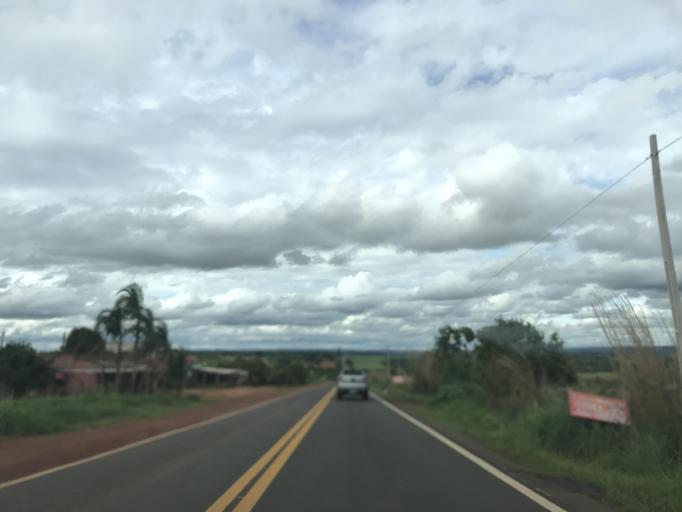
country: BR
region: Goias
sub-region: Piracanjuba
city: Piracanjuba
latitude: -17.2015
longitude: -48.7027
